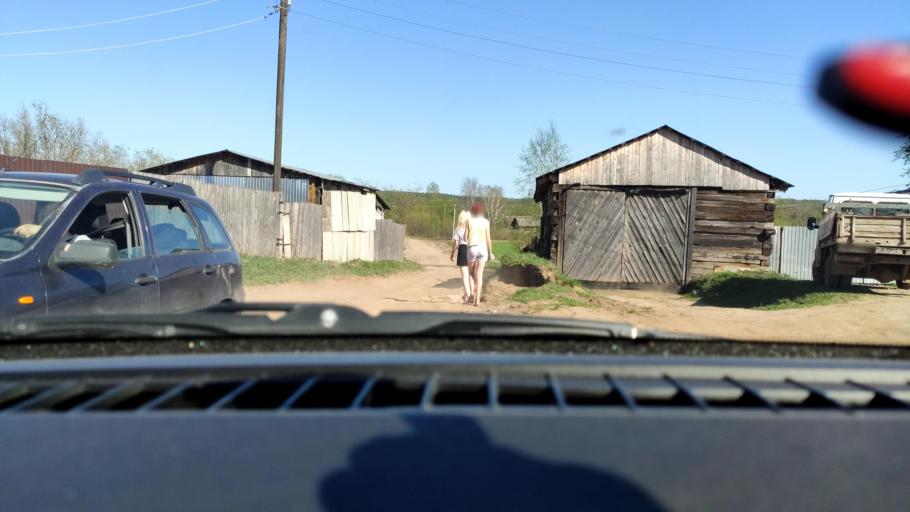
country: RU
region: Perm
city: Overyata
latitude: 58.0800
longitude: 55.9747
